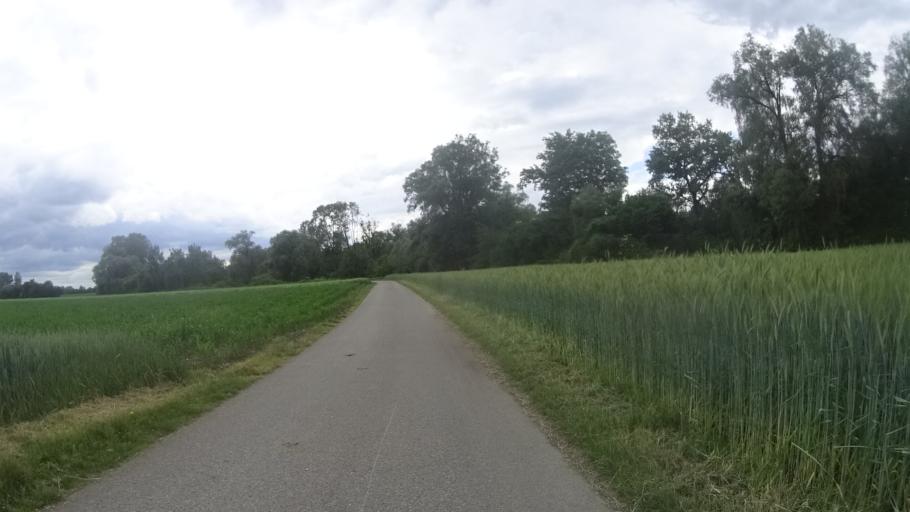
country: DE
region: Bavaria
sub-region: Upper Bavaria
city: Bergkirchen
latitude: 48.2382
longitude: 11.3695
